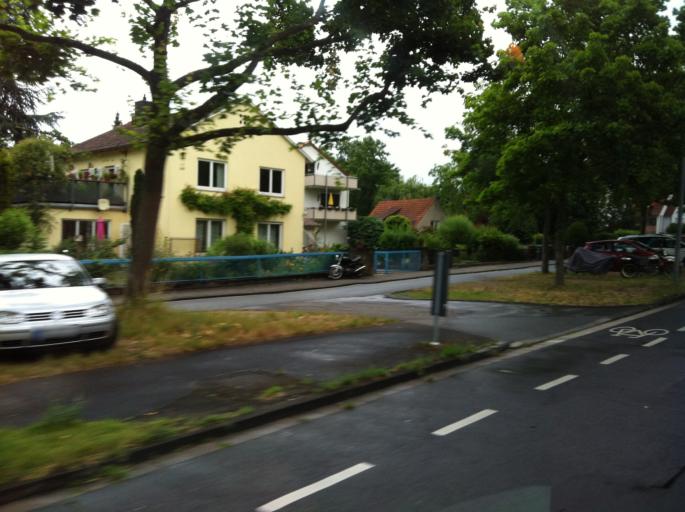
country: DE
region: Rheinland-Pfalz
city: Mainz
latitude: 50.0003
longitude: 8.2313
